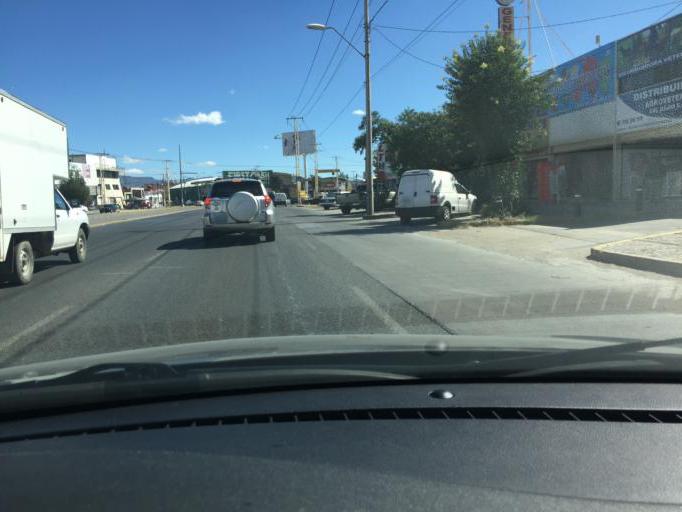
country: MX
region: Guanajuato
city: Leon
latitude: 21.1053
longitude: -101.7010
